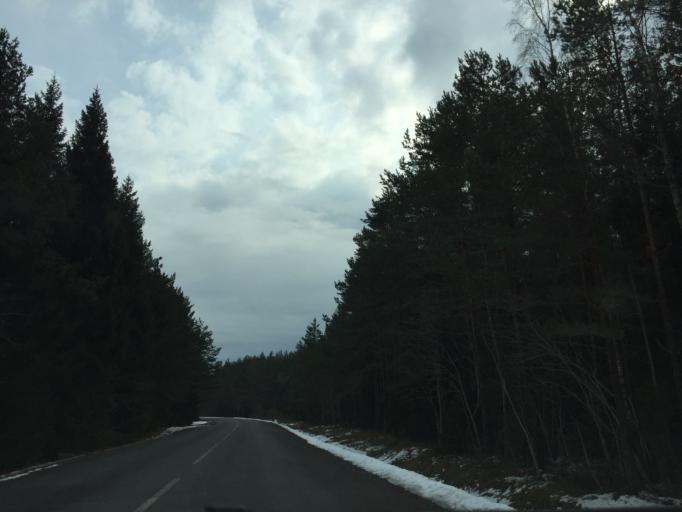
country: EE
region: Saare
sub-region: Kuressaare linn
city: Kuressaare
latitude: 58.4485
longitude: 22.0524
